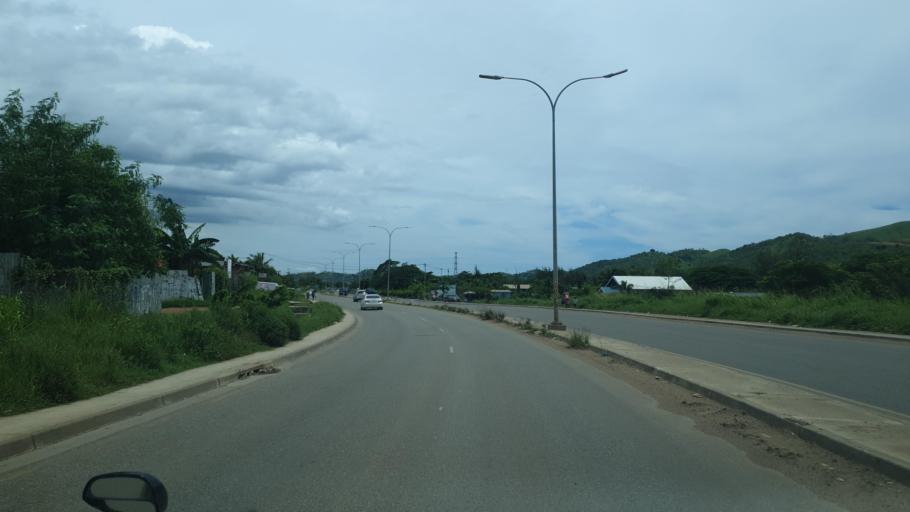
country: PG
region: National Capital
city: Port Moresby
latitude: -9.4910
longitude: 147.2200
